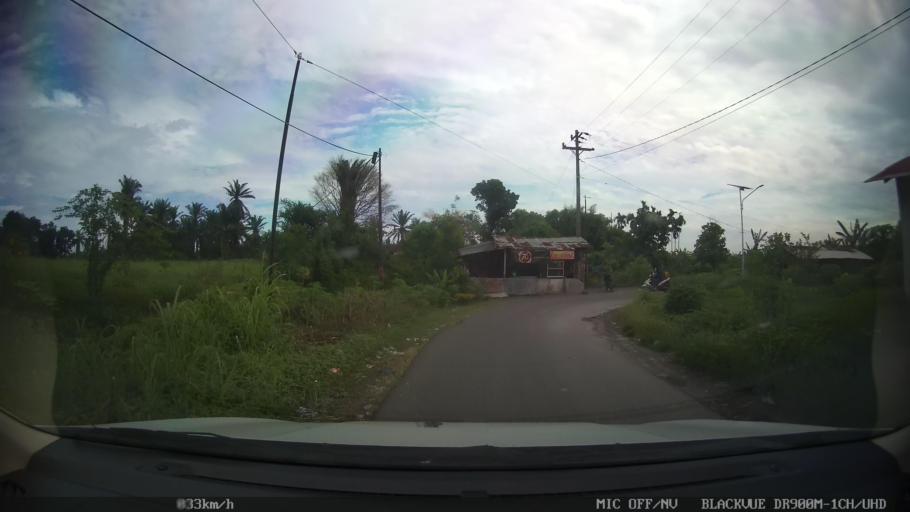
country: ID
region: North Sumatra
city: Sunggal
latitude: 3.5873
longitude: 98.5654
